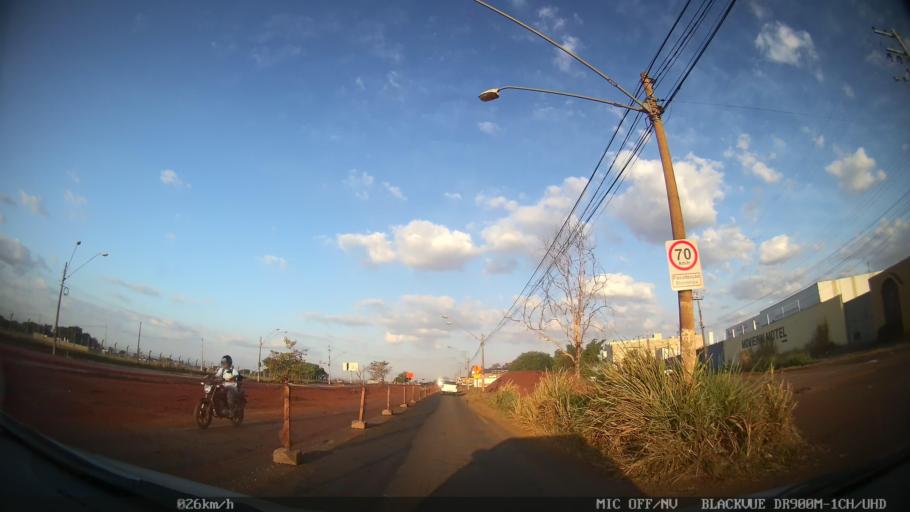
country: BR
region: Sao Paulo
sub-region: Ribeirao Preto
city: Ribeirao Preto
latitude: -21.1424
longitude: -47.7806
